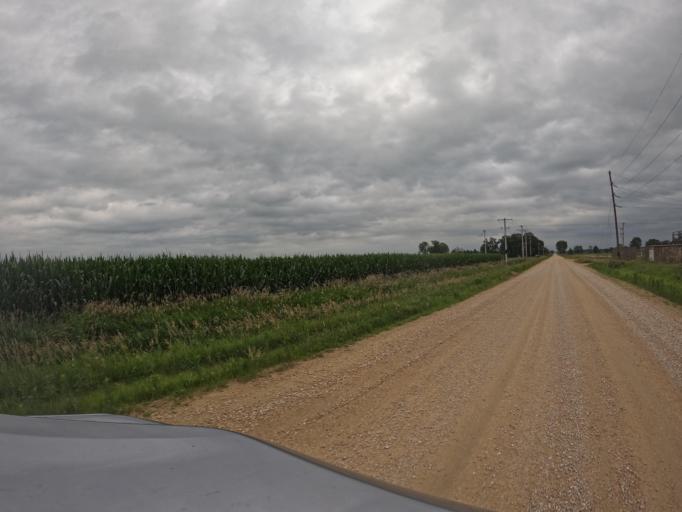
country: US
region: Iowa
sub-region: Clinton County
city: De Witt
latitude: 41.7863
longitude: -90.4531
